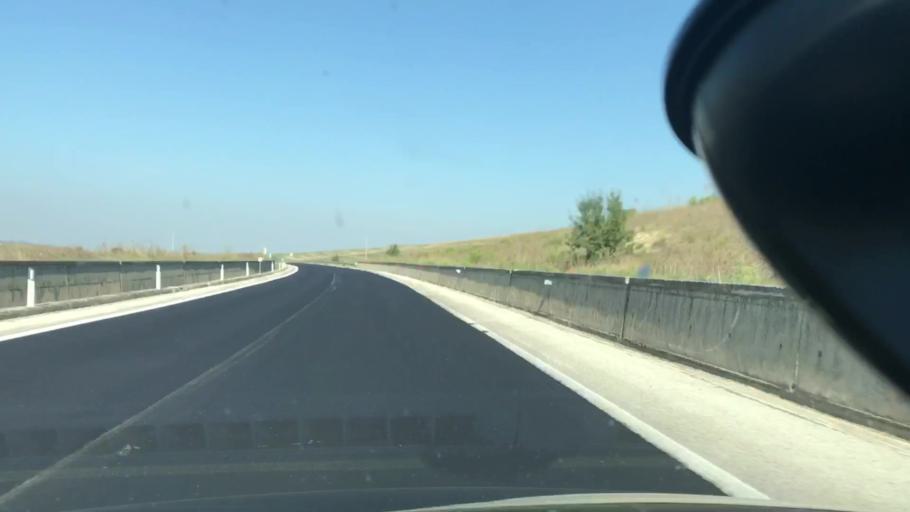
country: IT
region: Apulia
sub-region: Provincia di Barletta - Andria - Trani
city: Spinazzola
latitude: 40.9205
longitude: 16.0970
